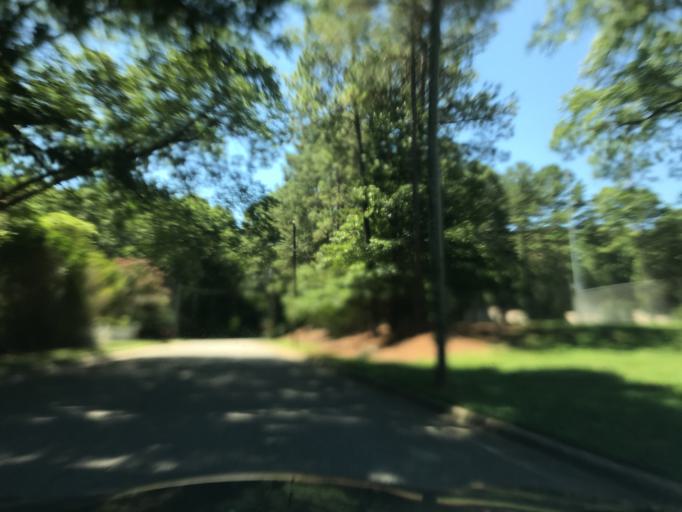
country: US
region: North Carolina
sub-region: Wake County
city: Raleigh
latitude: 35.7756
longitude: -78.6171
